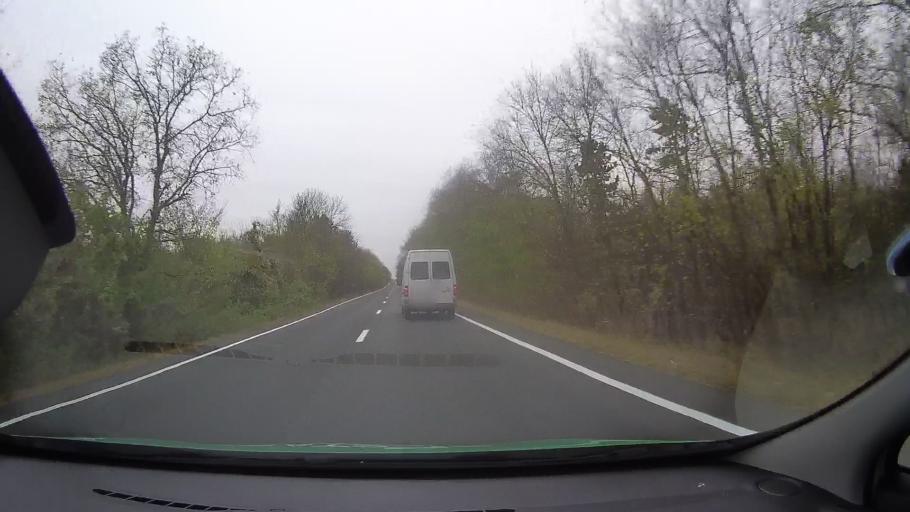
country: RO
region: Ialomita
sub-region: Comuna Mihail Kogalniceanu
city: Mihail Kogalniceanu
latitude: 44.6763
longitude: 27.7656
